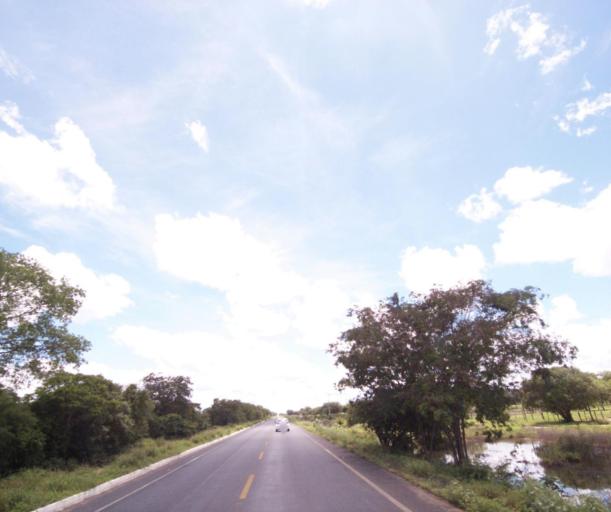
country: BR
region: Bahia
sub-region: Bom Jesus Da Lapa
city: Bom Jesus da Lapa
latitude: -13.2600
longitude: -43.4993
